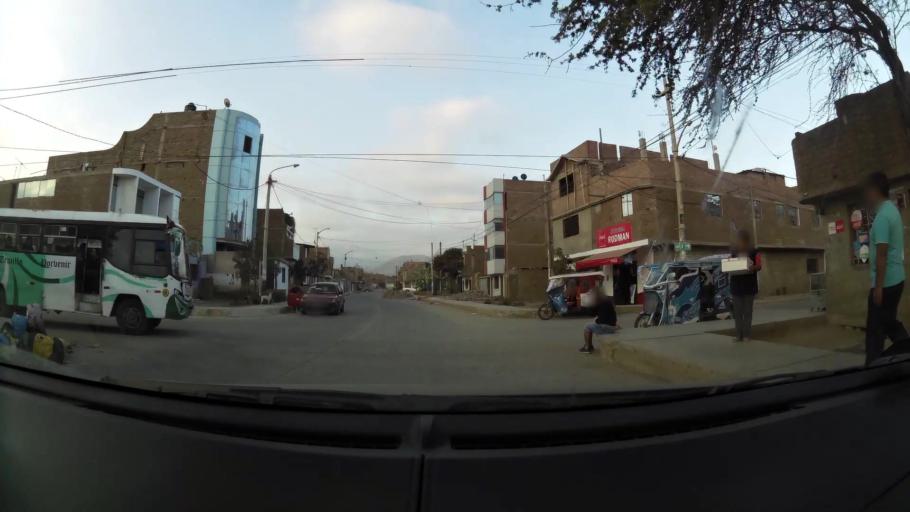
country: PE
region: La Libertad
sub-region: Provincia de Trujillo
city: El Porvenir
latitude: -8.0811
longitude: -79.0075
